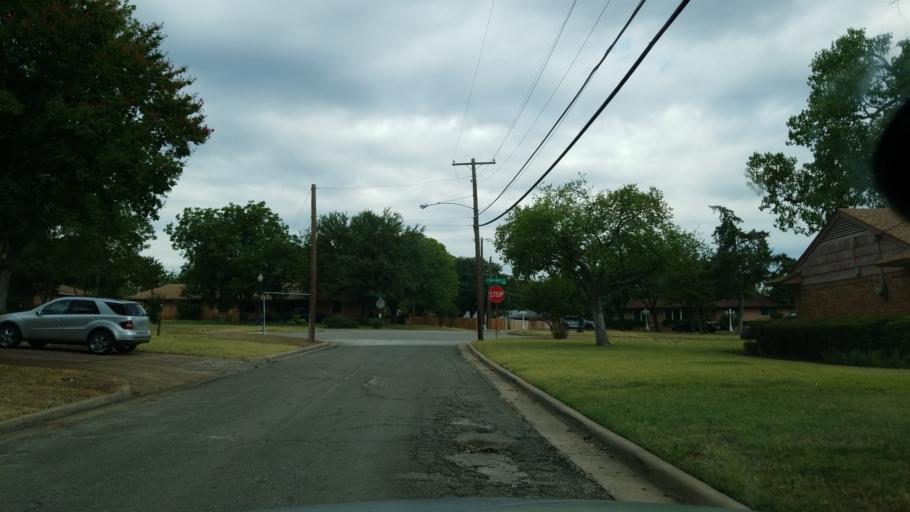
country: US
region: Texas
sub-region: Dallas County
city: Duncanville
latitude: 32.6721
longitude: -96.8449
